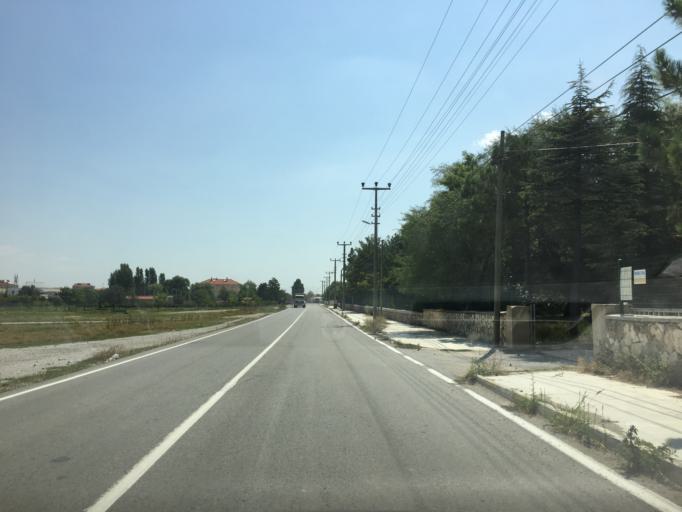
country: TR
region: Eskisehir
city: Cifteler
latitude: 39.3700
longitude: 31.0317
